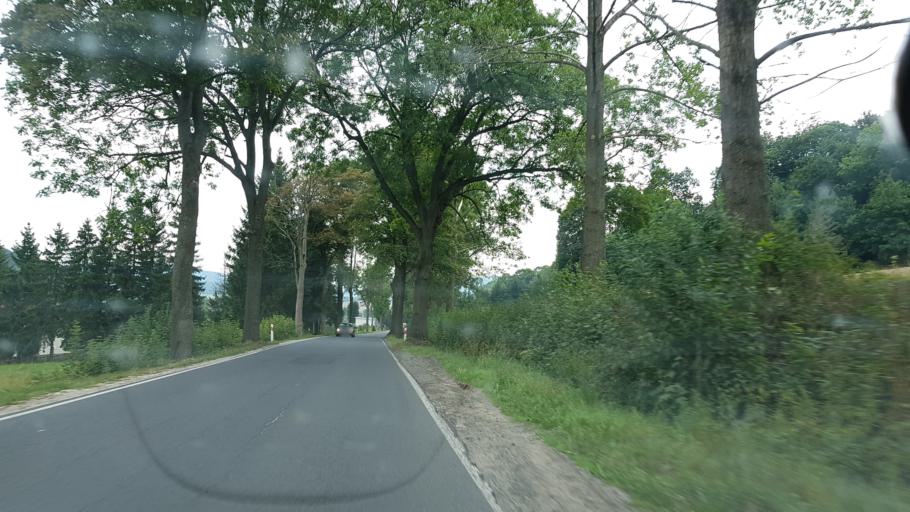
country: PL
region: Lower Silesian Voivodeship
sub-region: Powiat kamiennogorski
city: Marciszow
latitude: 50.8893
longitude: 15.9940
